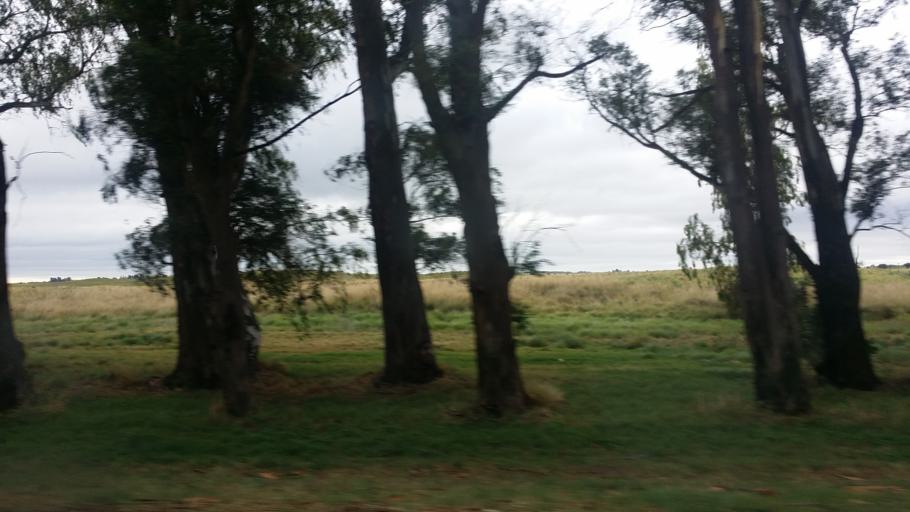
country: AR
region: La Pampa
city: Lonquimay
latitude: -36.4982
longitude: -63.6823
